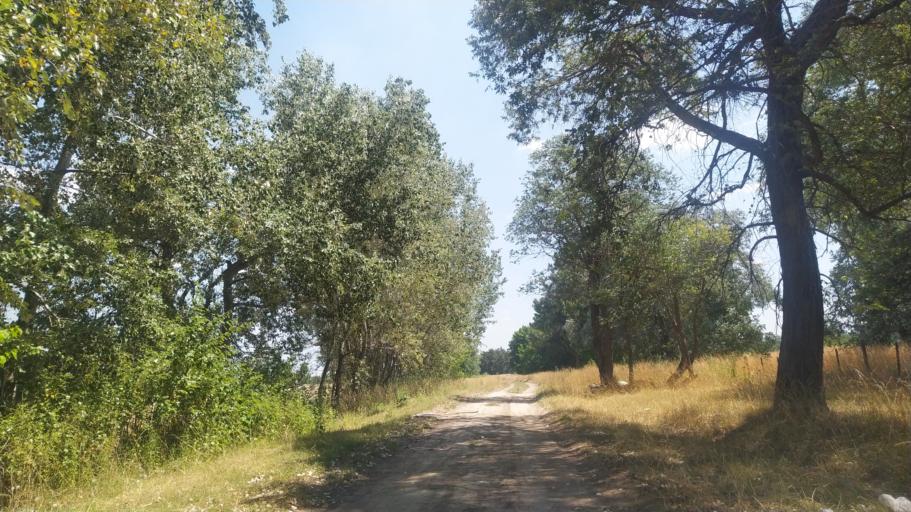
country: AR
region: Buenos Aires
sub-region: Partido de Ezeiza
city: Ezeiza
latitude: -34.9090
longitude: -58.6267
